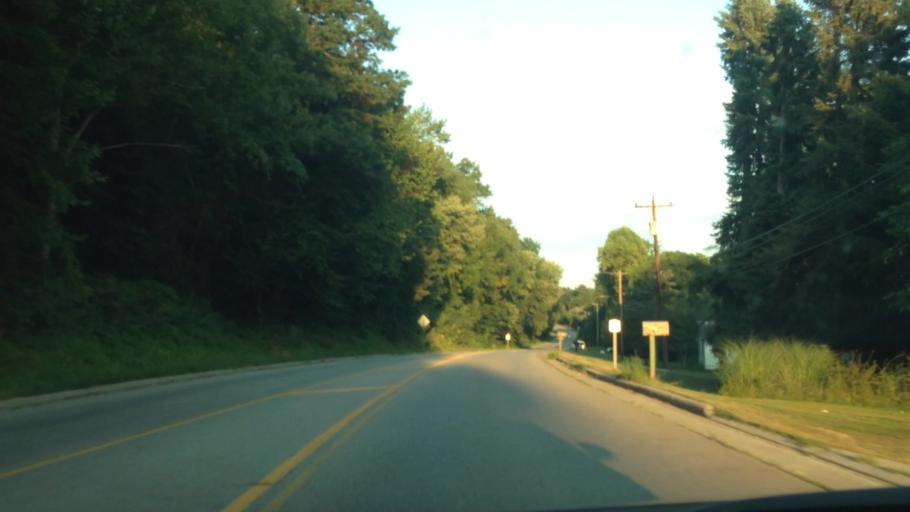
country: US
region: Ohio
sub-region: Summit County
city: Portage Lakes
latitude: 40.9830
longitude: -81.5586
